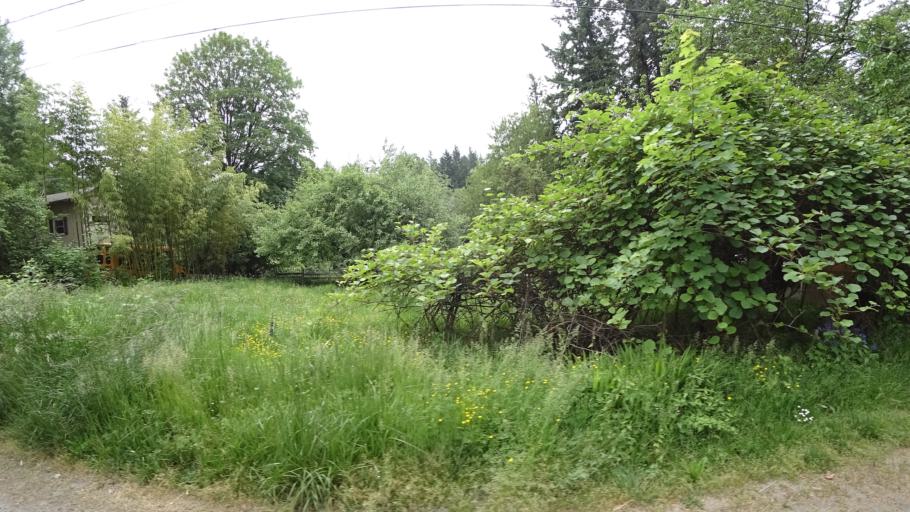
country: US
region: Oregon
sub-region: Washington County
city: Garden Home-Whitford
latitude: 45.4700
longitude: -122.7334
